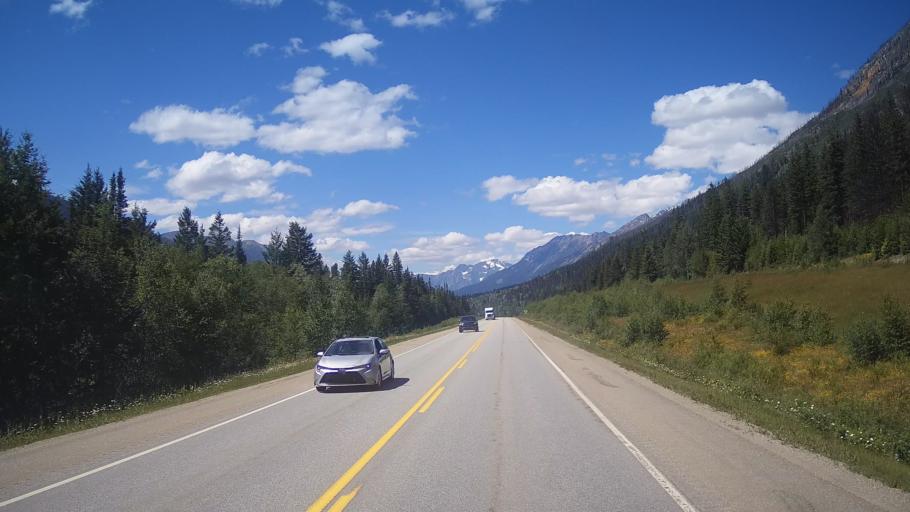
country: CA
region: Alberta
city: Jasper Park Lodge
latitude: 52.9642
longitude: -118.9169
